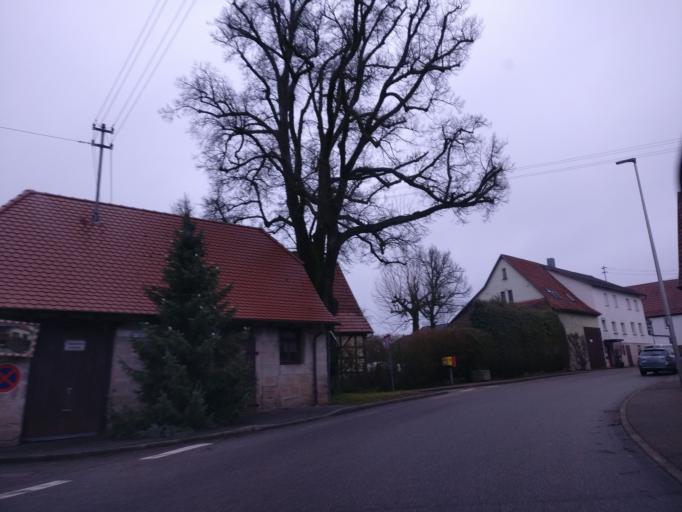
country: DE
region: Baden-Wuerttemberg
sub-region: Regierungsbezirk Stuttgart
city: Rudersberg
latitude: 48.8549
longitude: 9.5017
